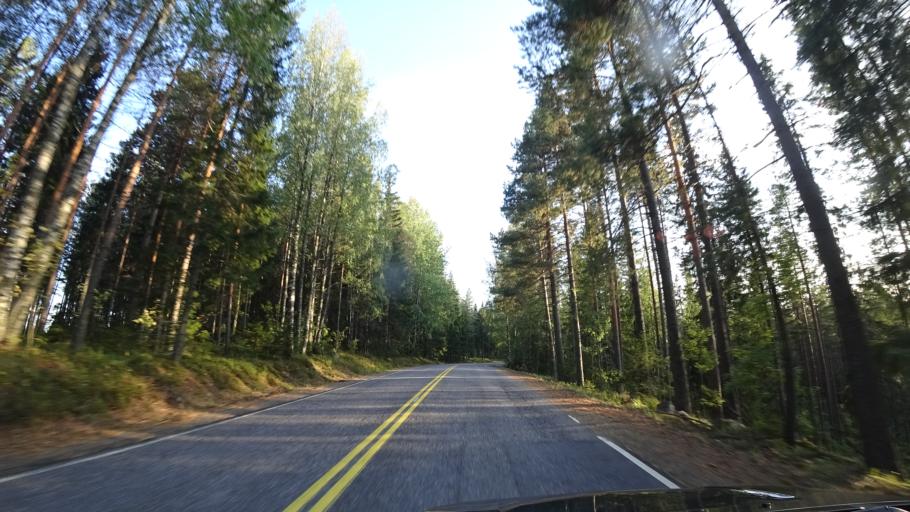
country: FI
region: Haeme
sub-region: Haemeenlinna
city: Tuulos
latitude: 60.9957
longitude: 24.8316
